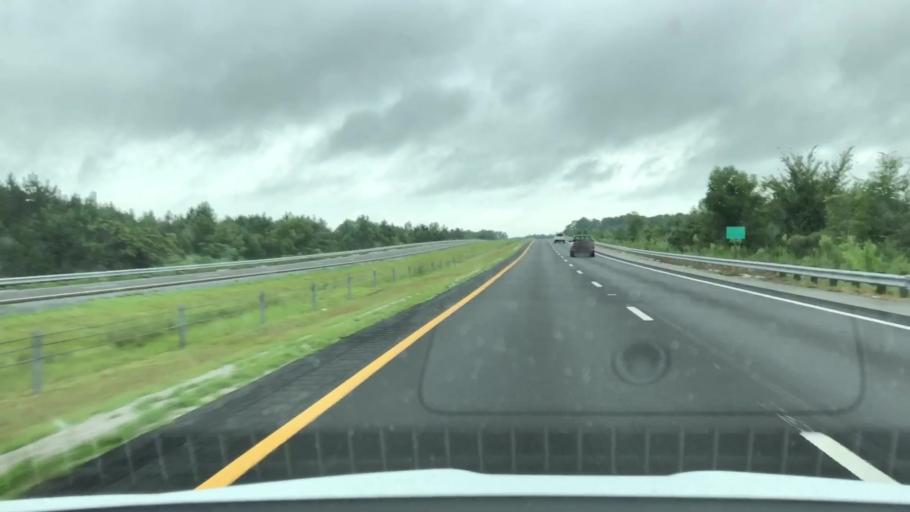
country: US
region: North Carolina
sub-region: Wayne County
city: Goldsboro
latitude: 35.4653
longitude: -77.9860
